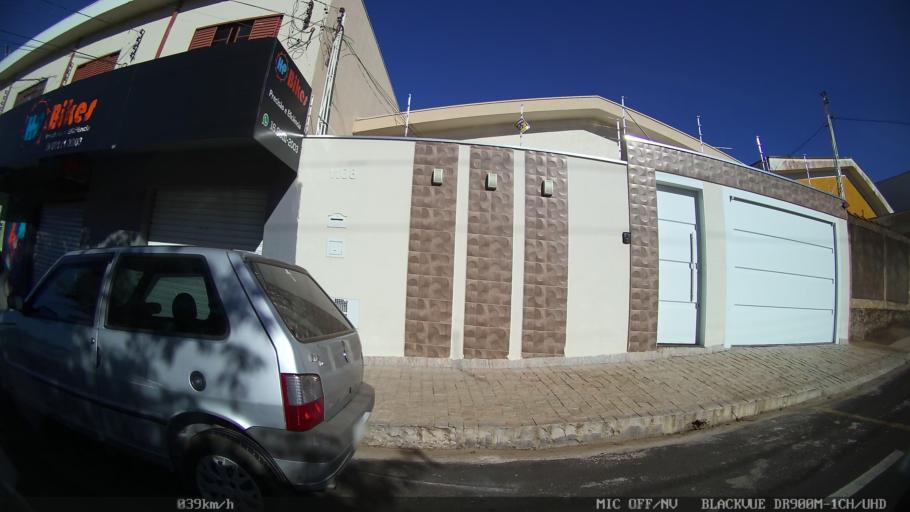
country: BR
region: Sao Paulo
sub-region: Franca
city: Franca
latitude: -20.5456
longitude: -47.4109
